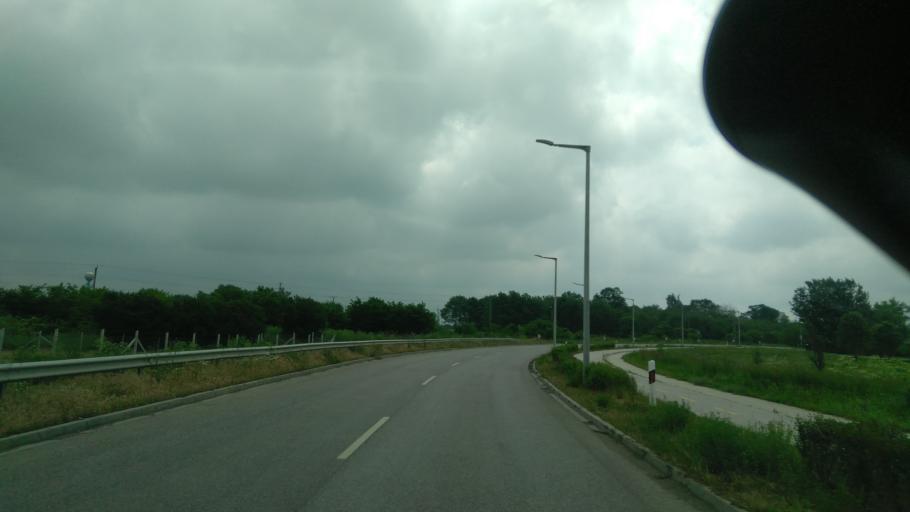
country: HU
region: Bekes
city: Bekescsaba
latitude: 46.6535
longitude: 21.0907
